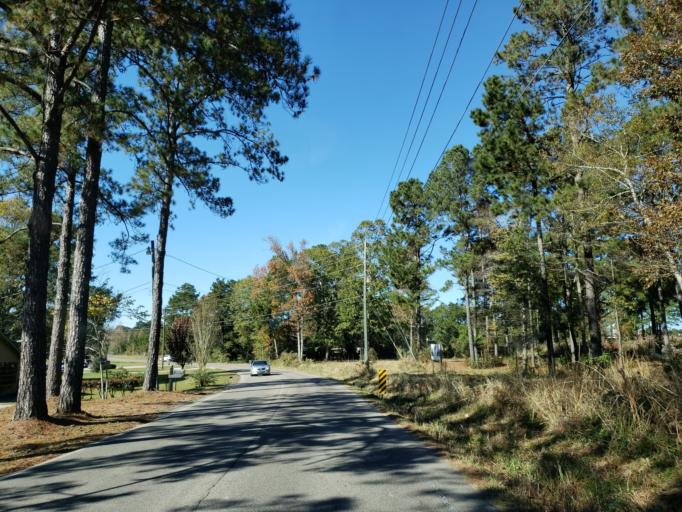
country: US
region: Mississippi
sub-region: Lamar County
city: West Hattiesburg
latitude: 31.3021
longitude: -89.3784
